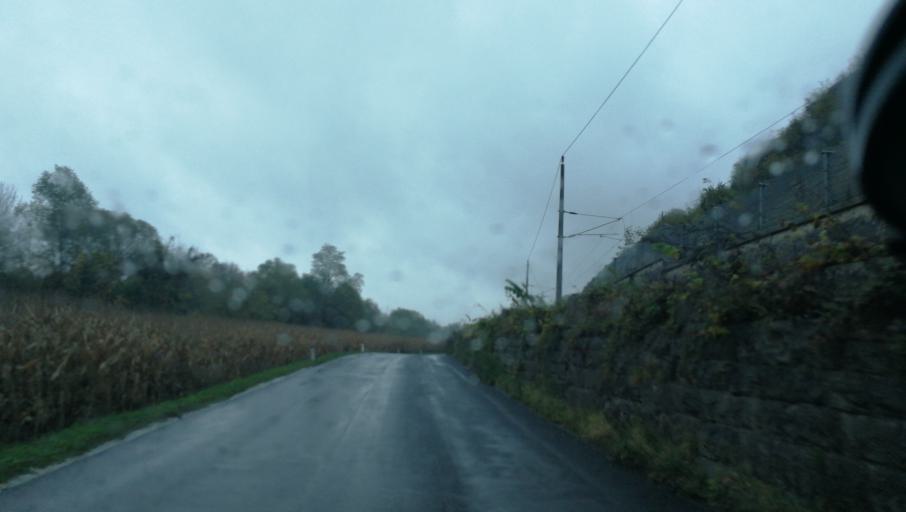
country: AT
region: Styria
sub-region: Politischer Bezirk Leibnitz
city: Ehrenhausen
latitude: 46.7243
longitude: 15.5985
